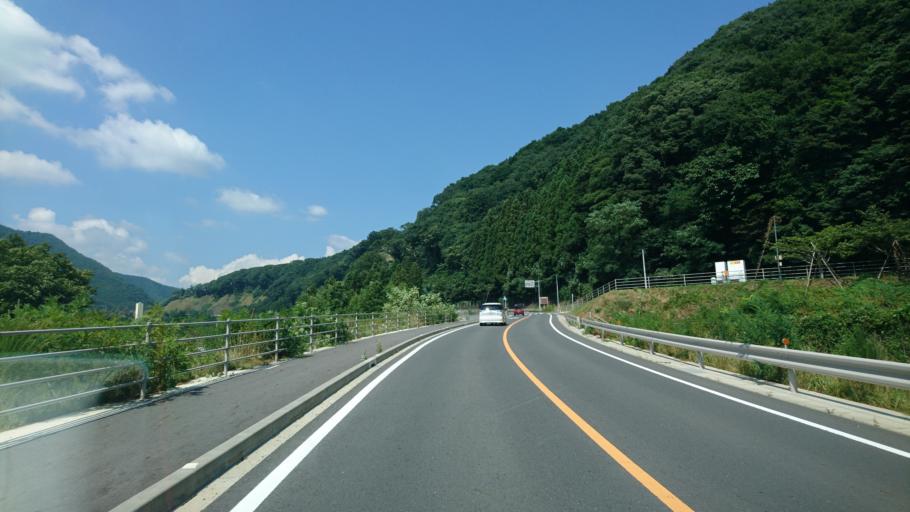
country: JP
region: Gunma
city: Numata
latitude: 36.7610
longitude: 139.2283
